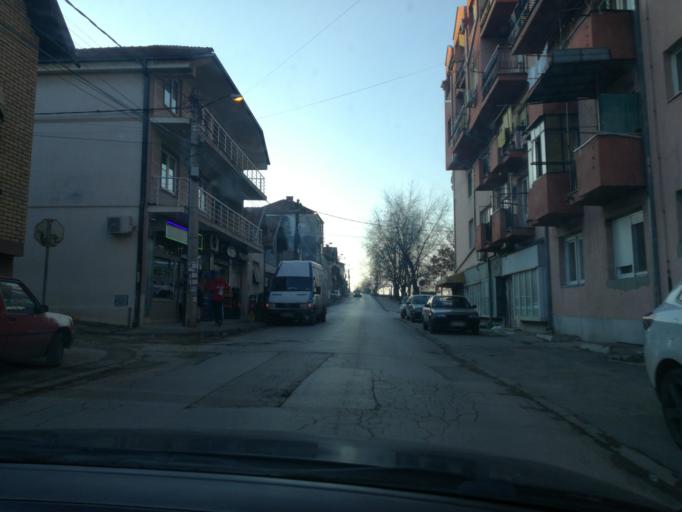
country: RS
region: Central Serbia
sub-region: Nisavski Okrug
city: Nis
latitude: 43.3110
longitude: 21.8854
